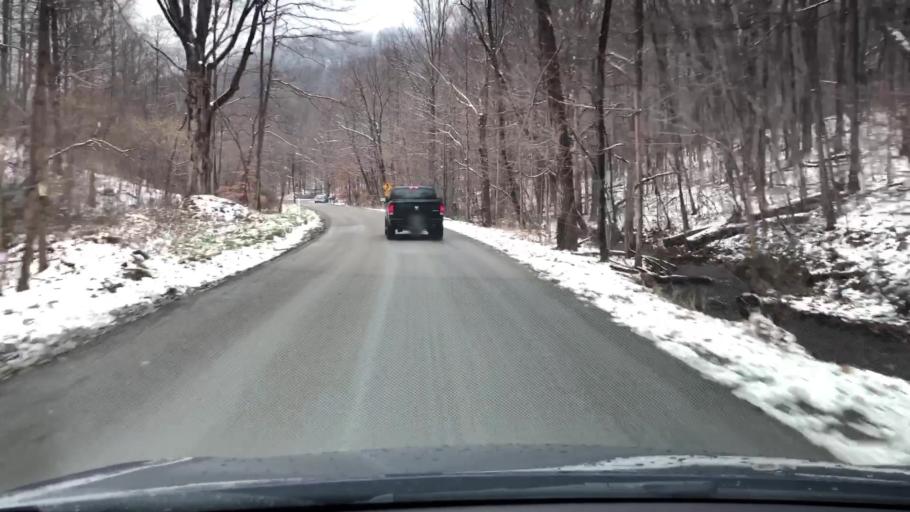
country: US
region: Pennsylvania
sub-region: Fayette County
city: South Connellsville
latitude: 39.9345
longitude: -79.5637
